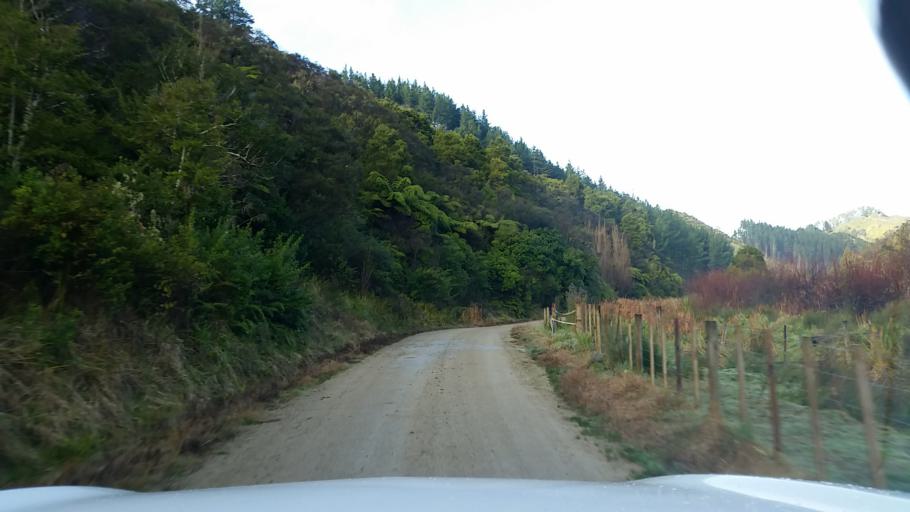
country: NZ
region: Taranaki
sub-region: South Taranaki District
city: Patea
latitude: -39.6791
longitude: 174.7653
